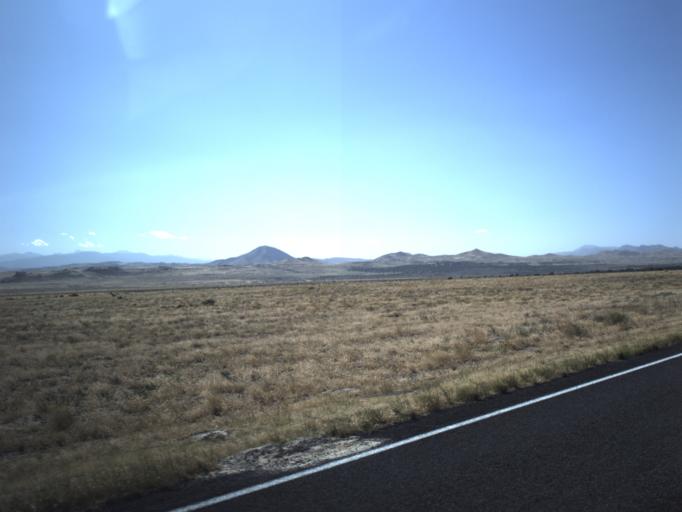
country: US
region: Utah
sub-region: Beaver County
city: Milford
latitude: 38.8521
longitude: -112.8417
